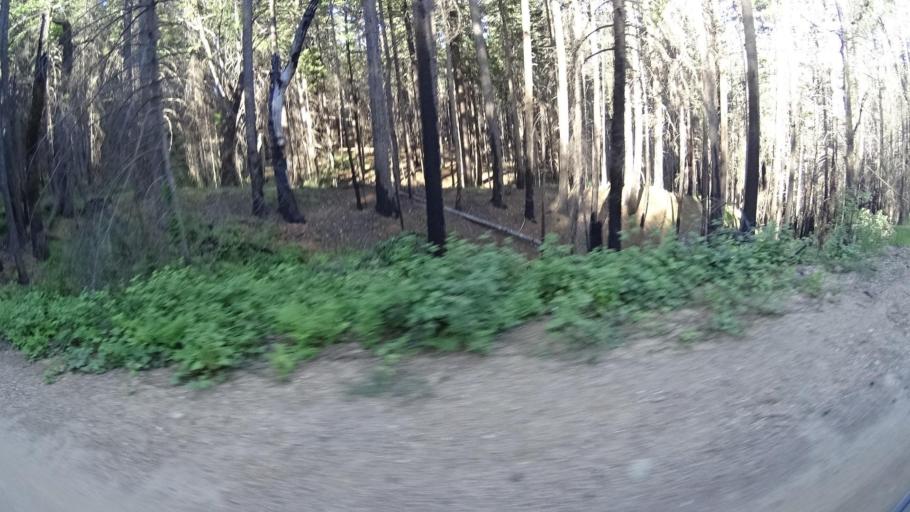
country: US
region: California
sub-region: Lake County
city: Upper Lake
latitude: 39.3644
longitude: -122.9915
